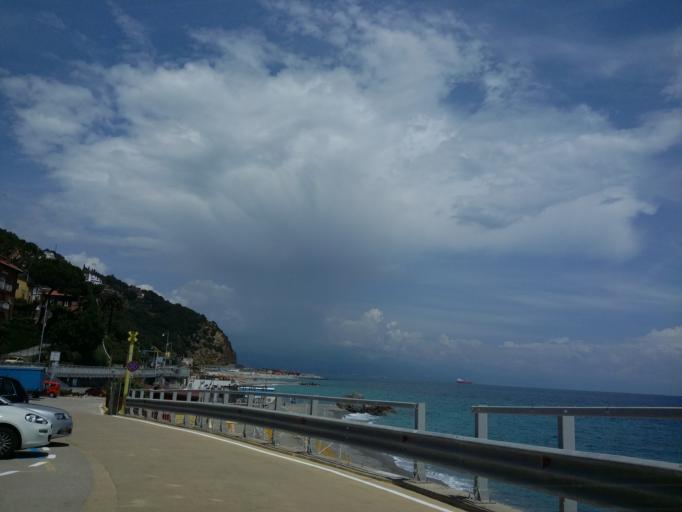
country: IT
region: Liguria
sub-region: Provincia di Savona
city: Bergeggi
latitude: 44.2453
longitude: 8.4442
